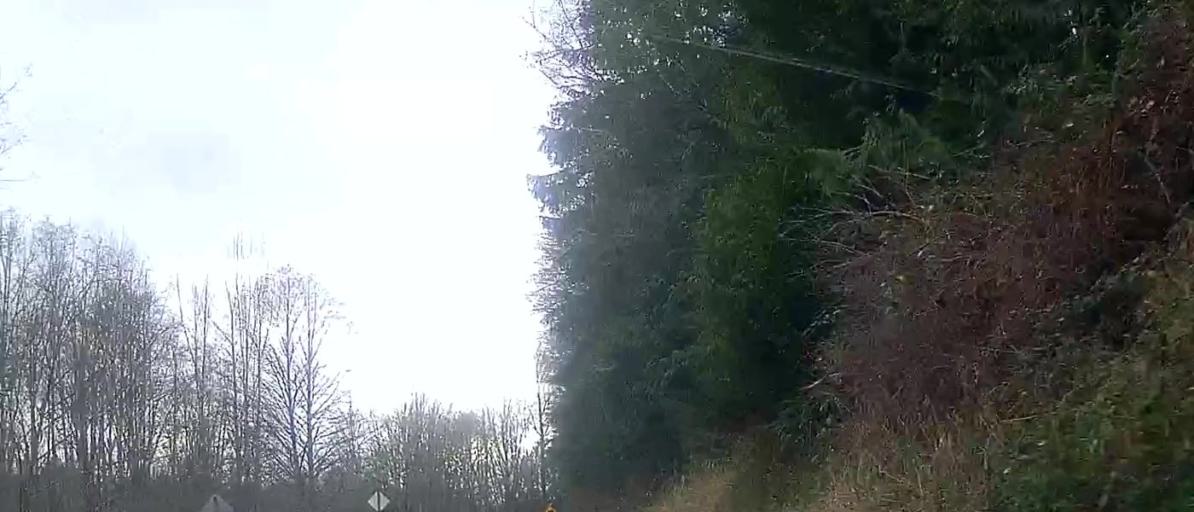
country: US
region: Washington
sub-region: Skagit County
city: Sedro-Woolley
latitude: 48.5852
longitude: -122.2434
